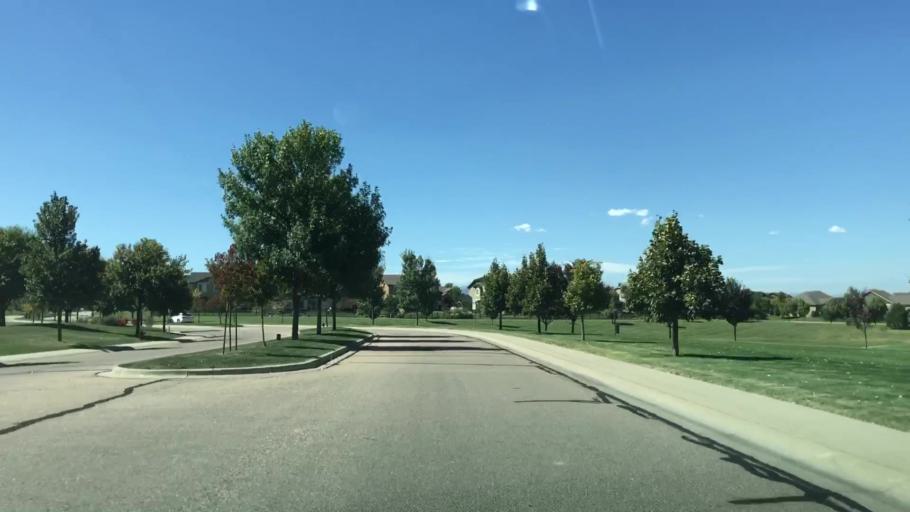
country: US
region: Colorado
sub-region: Weld County
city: Windsor
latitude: 40.4508
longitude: -104.9458
